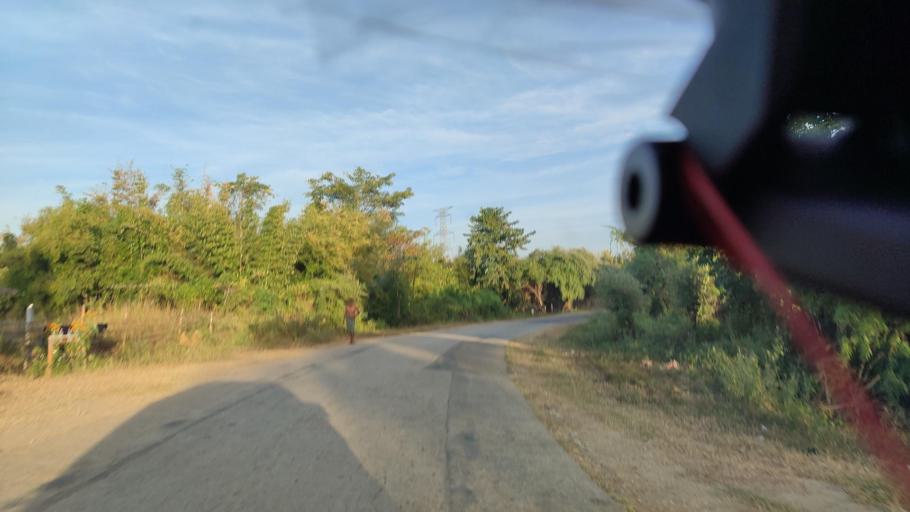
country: MM
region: Mandalay
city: Nay Pyi Taw
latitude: 19.9844
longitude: 95.9625
